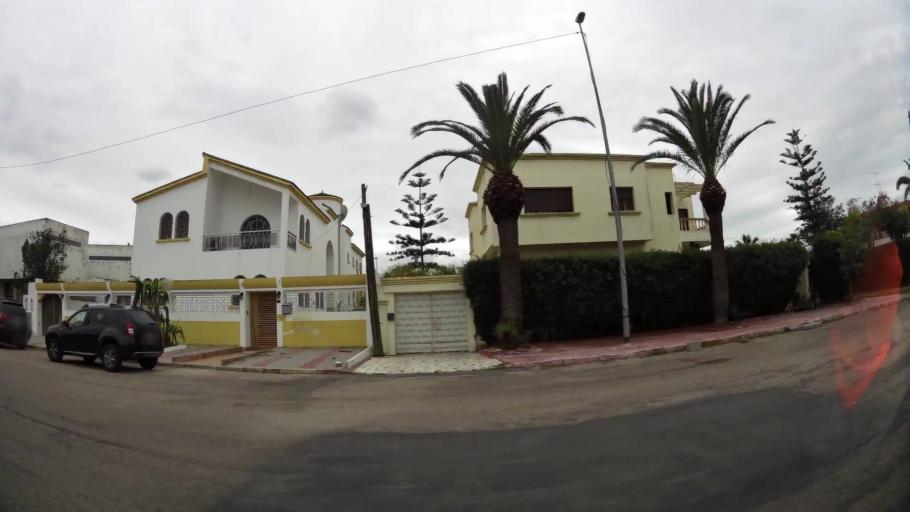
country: MA
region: Grand Casablanca
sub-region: Casablanca
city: Casablanca
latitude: 33.5621
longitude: -7.6240
